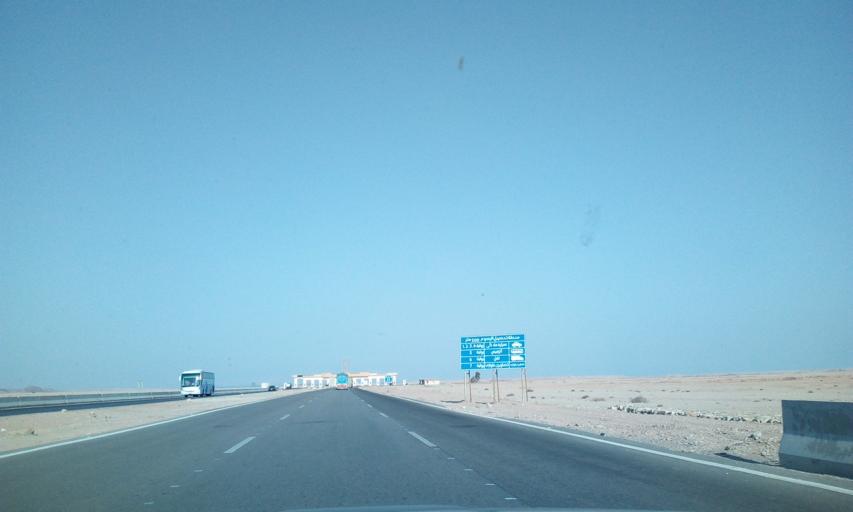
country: EG
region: As Suways
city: Ain Sukhna
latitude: 29.1102
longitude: 32.5435
